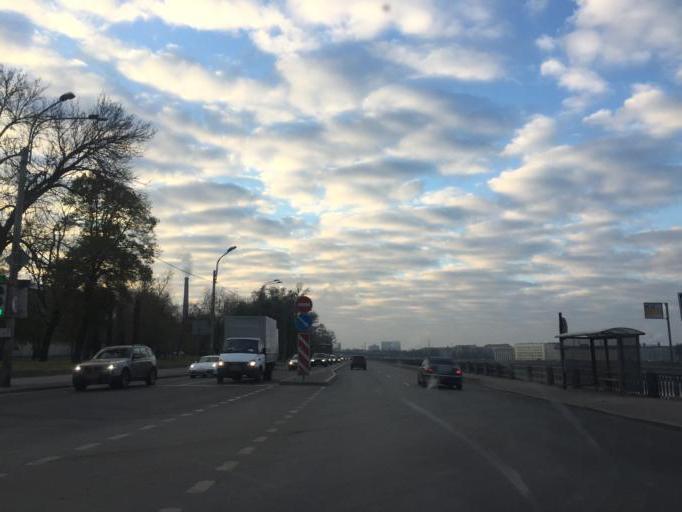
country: RU
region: St.-Petersburg
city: Obukhovo
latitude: 59.8885
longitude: 30.4483
